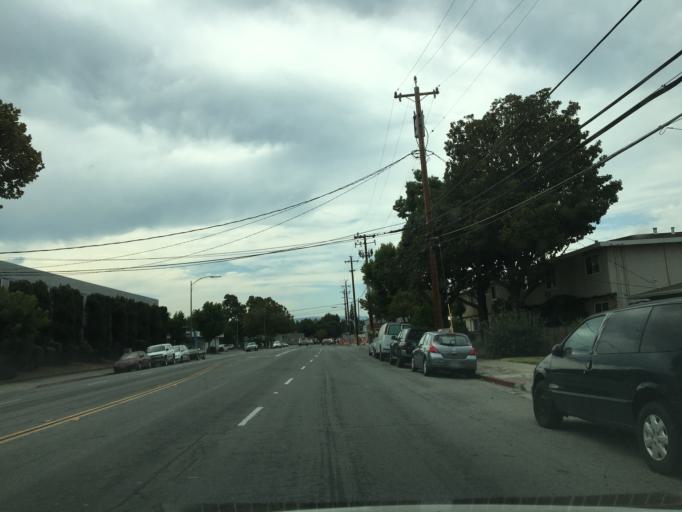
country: US
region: California
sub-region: Santa Clara County
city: Burbank
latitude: 37.3108
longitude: -121.9295
